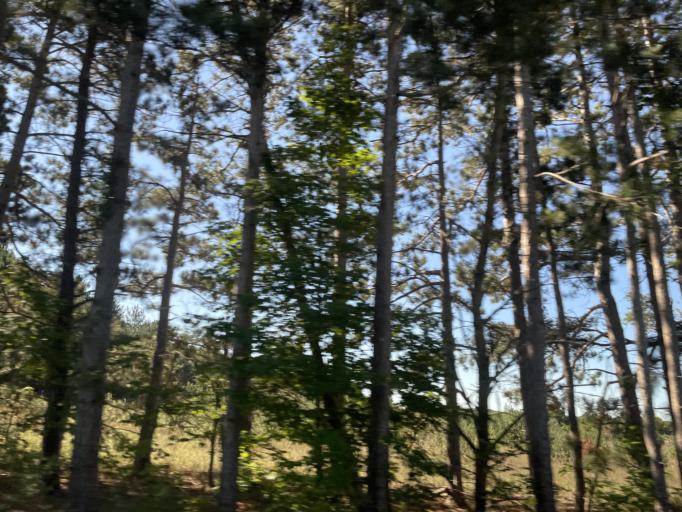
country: US
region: Michigan
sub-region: Benzie County
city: Beulah
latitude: 44.6173
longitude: -86.0643
